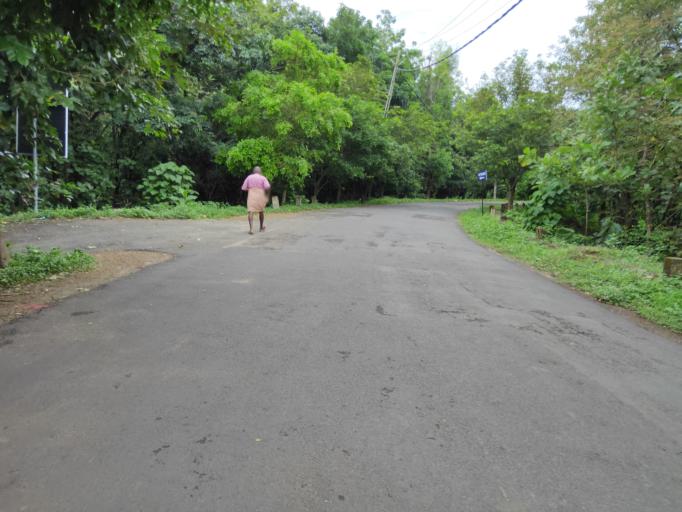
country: IN
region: Kerala
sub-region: Malappuram
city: Manjeri
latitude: 11.2642
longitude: 76.2393
